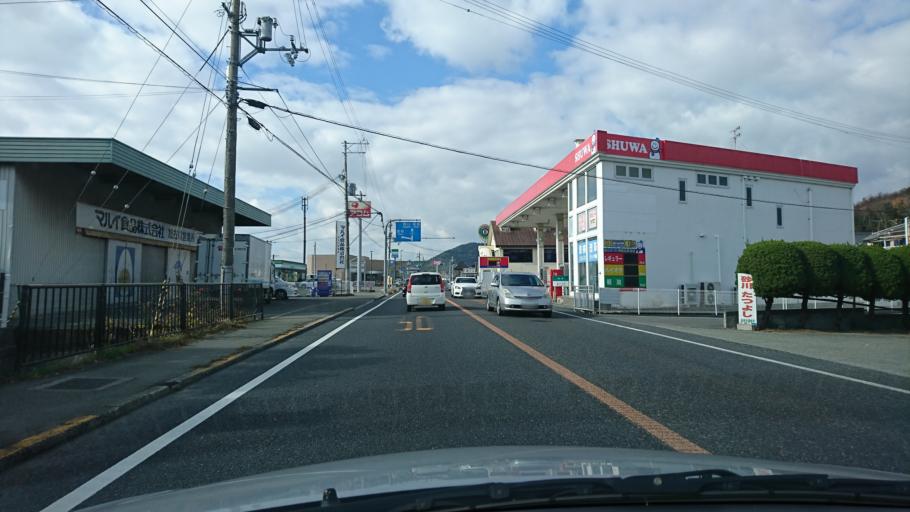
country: JP
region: Hyogo
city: Kakogawacho-honmachi
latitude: 34.7916
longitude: 134.7948
